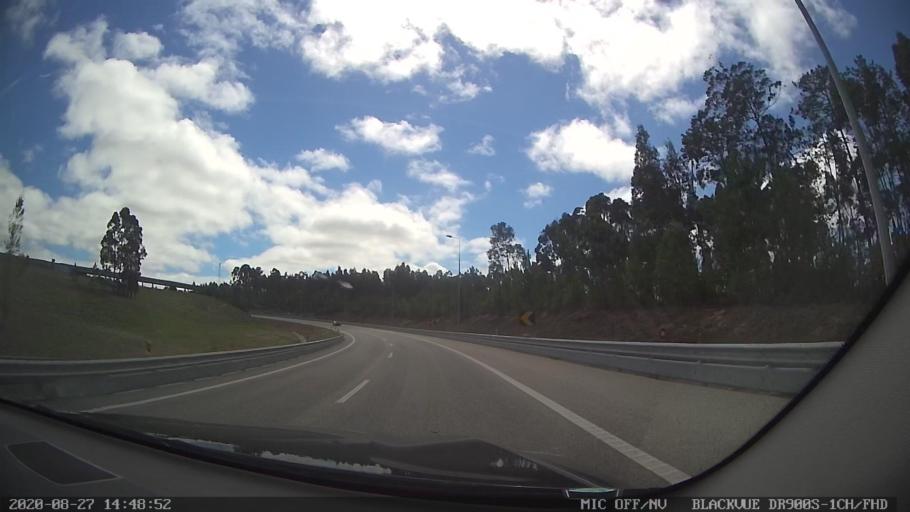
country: PT
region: Leiria
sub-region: Marinha Grande
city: Marinha Grande
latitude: 39.7417
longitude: -8.8864
